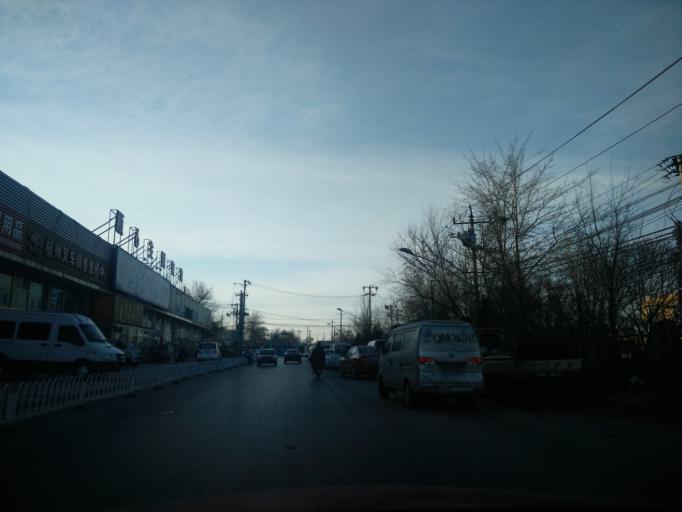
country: CN
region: Beijing
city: Huaxiang
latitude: 39.8187
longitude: 116.3475
